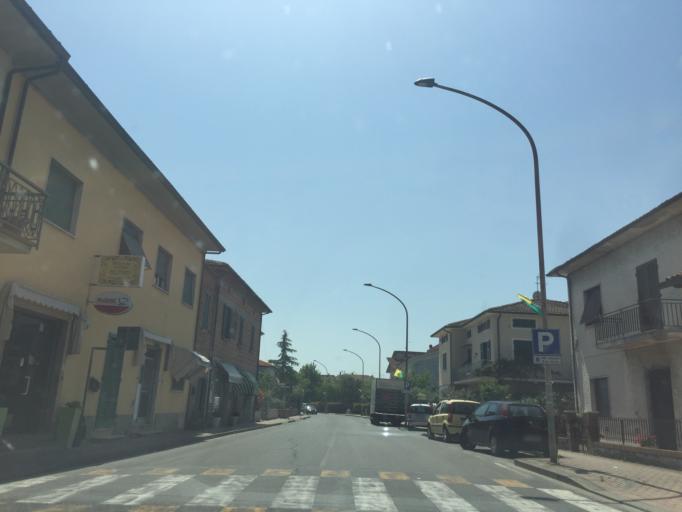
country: IT
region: Tuscany
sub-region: Provincia di Pistoia
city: Ponte Buggianese
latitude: 43.8389
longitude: 10.7480
